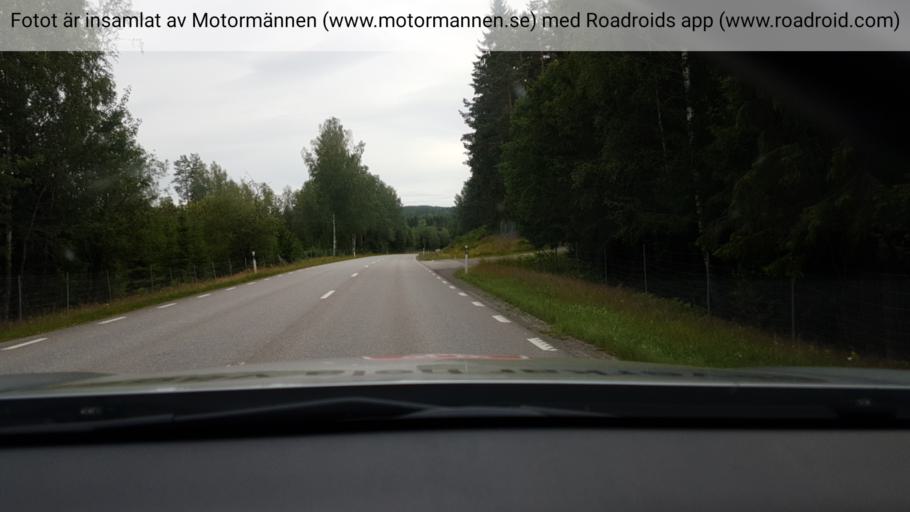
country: SE
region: Vaestra Goetaland
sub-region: Bengtsfors Kommun
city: Billingsfors
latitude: 58.9627
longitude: 12.2331
